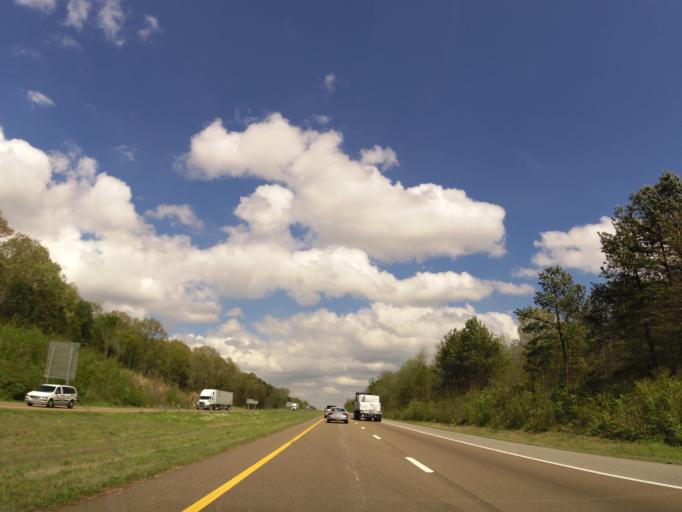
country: US
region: Tennessee
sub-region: Shelby County
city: Arlington
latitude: 35.2731
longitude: -89.6440
